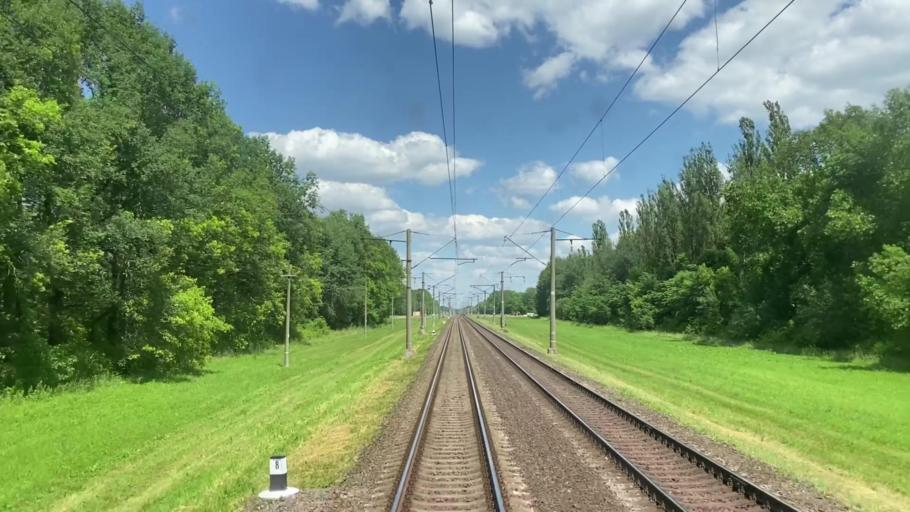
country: BY
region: Brest
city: Zhabinka
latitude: 52.2500
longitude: 24.1165
